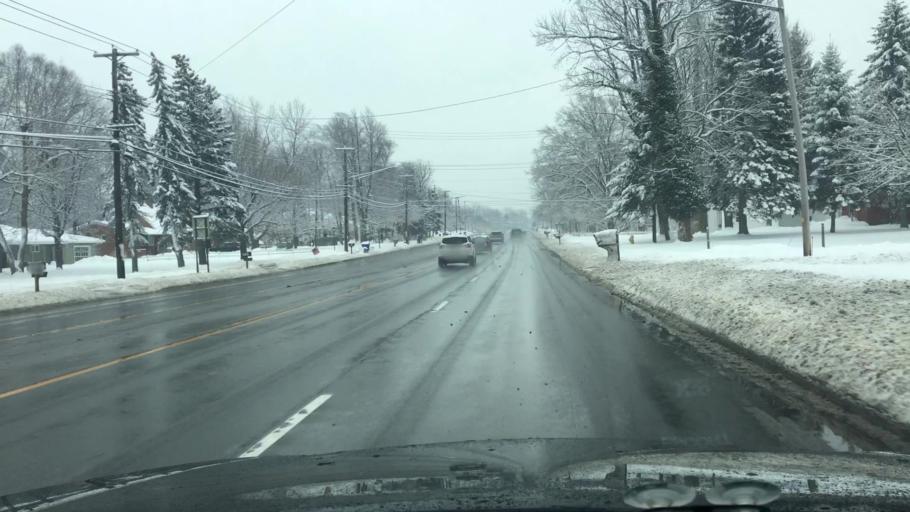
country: US
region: New York
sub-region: Erie County
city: Orchard Park
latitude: 42.8166
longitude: -78.7525
